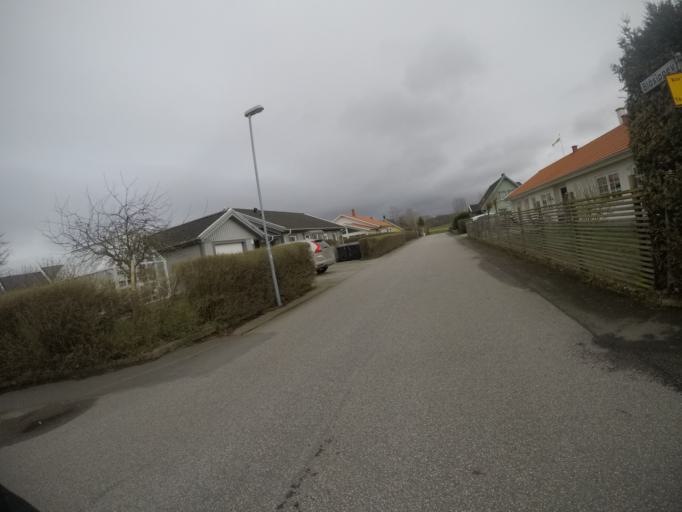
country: SE
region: Halland
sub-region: Laholms Kommun
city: Laholm
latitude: 56.5043
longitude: 13.0491
